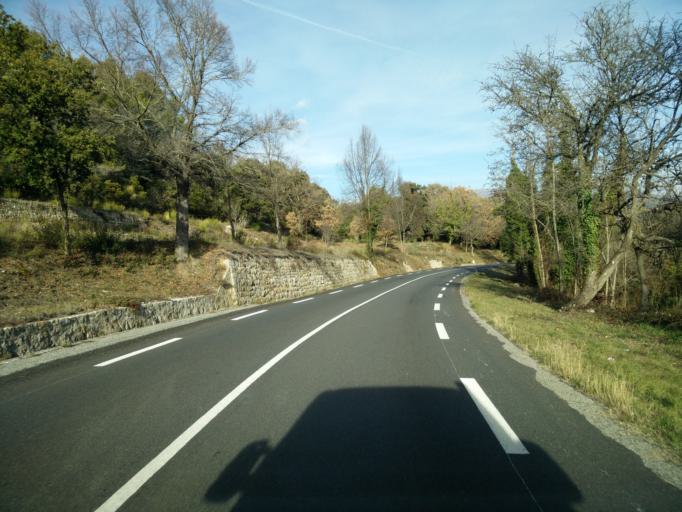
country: FR
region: Provence-Alpes-Cote d'Azur
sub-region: Departement du Var
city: Montauroux
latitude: 43.6053
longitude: 6.8075
